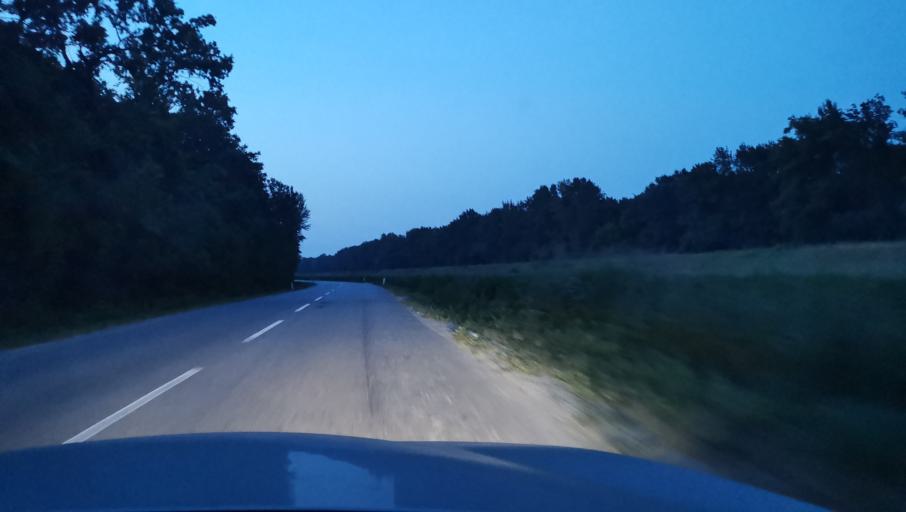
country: RS
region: Central Serbia
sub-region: Belgrade
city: Obrenovac
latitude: 44.6926
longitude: 20.1981
